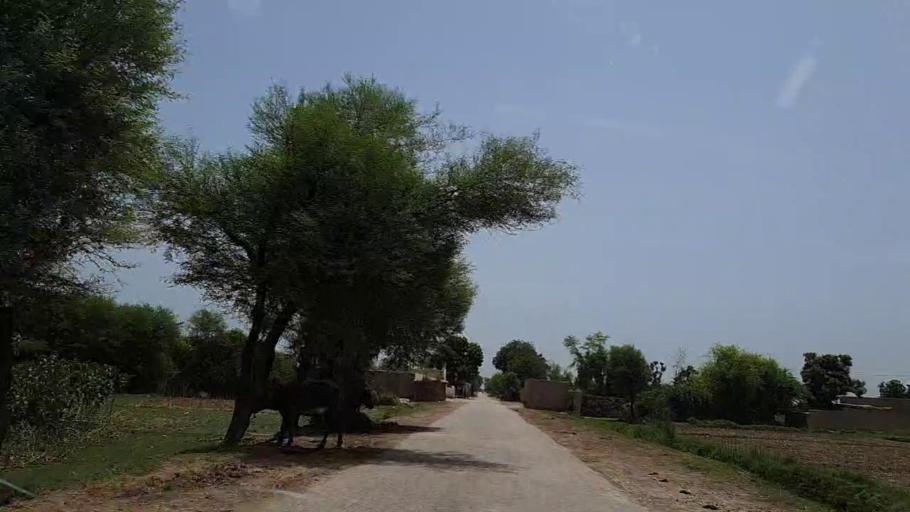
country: PK
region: Sindh
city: Tharu Shah
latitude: 26.9589
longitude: 68.0682
